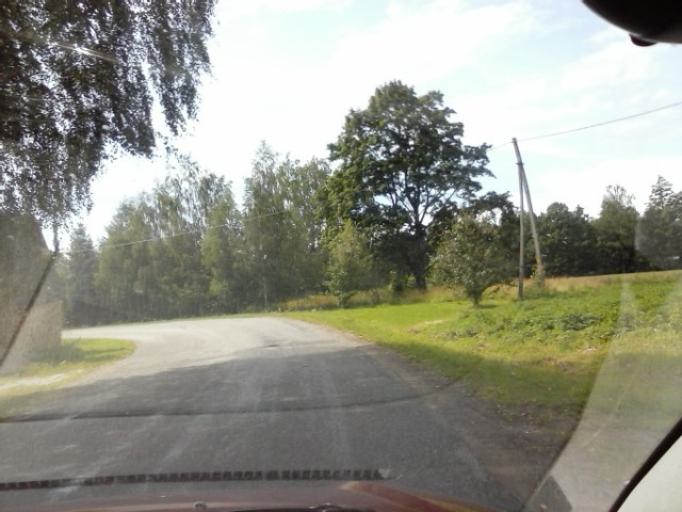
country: EE
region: Polvamaa
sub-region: Polva linn
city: Polva
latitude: 58.2638
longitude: 27.0010
